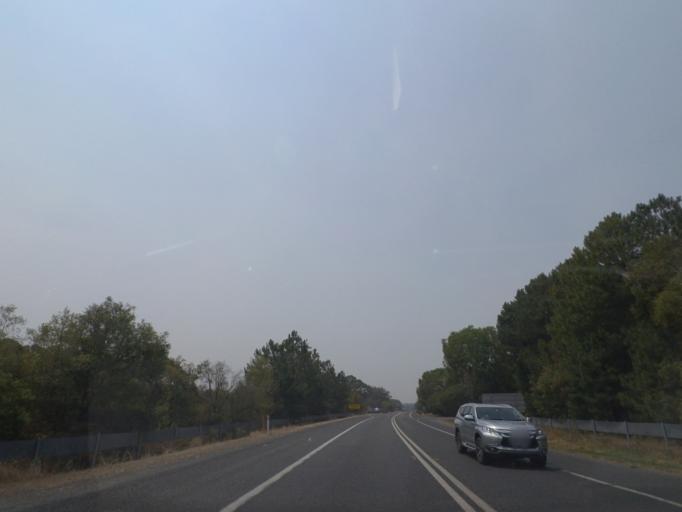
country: AU
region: New South Wales
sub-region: Ballina
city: Ballina
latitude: -28.9367
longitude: 153.4710
